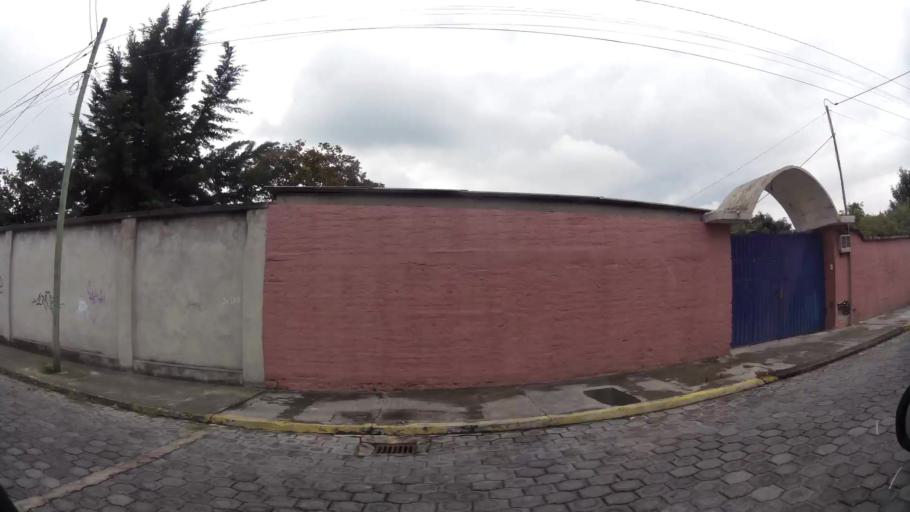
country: EC
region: Pichincha
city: Sangolqui
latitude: -0.3042
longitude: -78.4723
